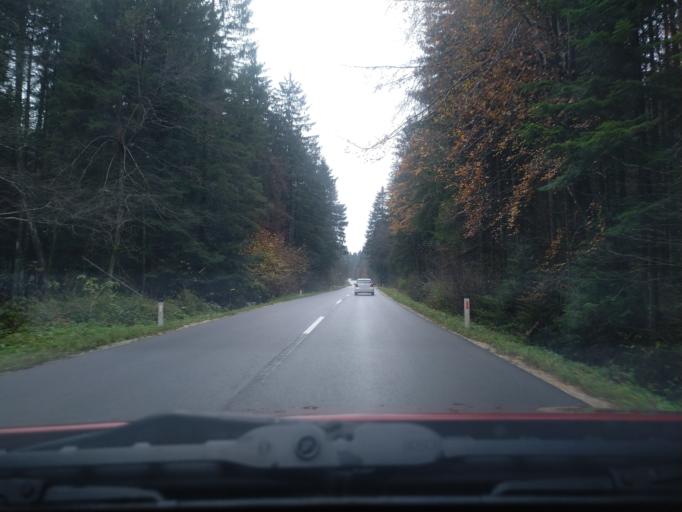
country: SI
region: Ljubno
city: Ljubno ob Savinji
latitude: 46.3151
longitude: 14.8458
